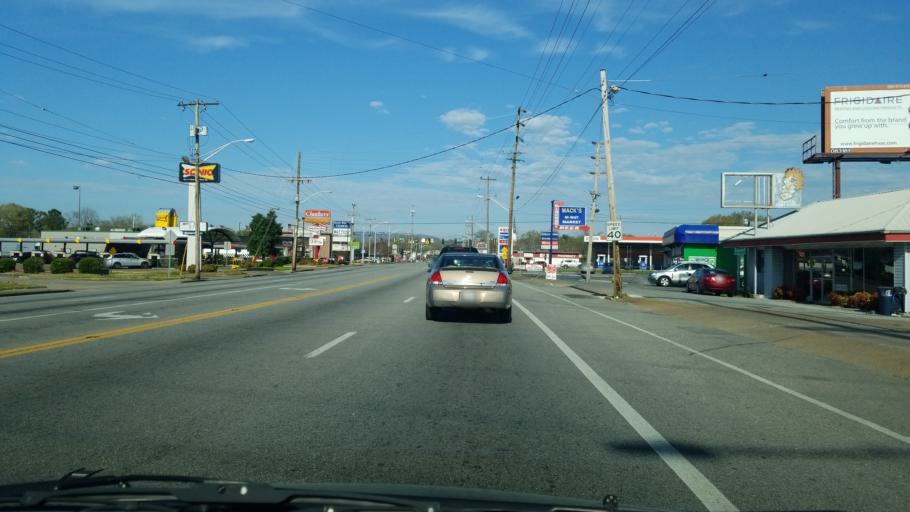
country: US
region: Tennessee
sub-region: Hamilton County
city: East Ridge
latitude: 34.9955
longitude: -85.2356
